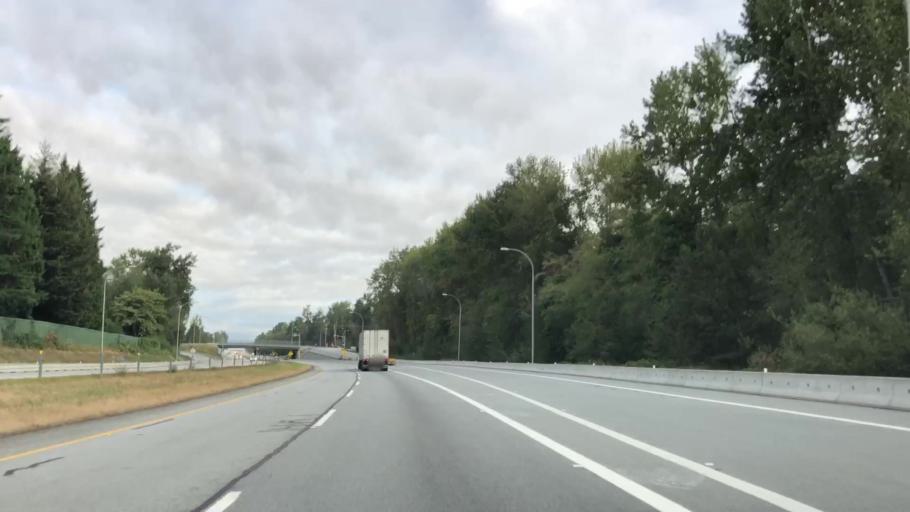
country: CA
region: British Columbia
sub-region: Greater Vancouver Regional District
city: White Rock
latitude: 49.0277
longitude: -122.7657
